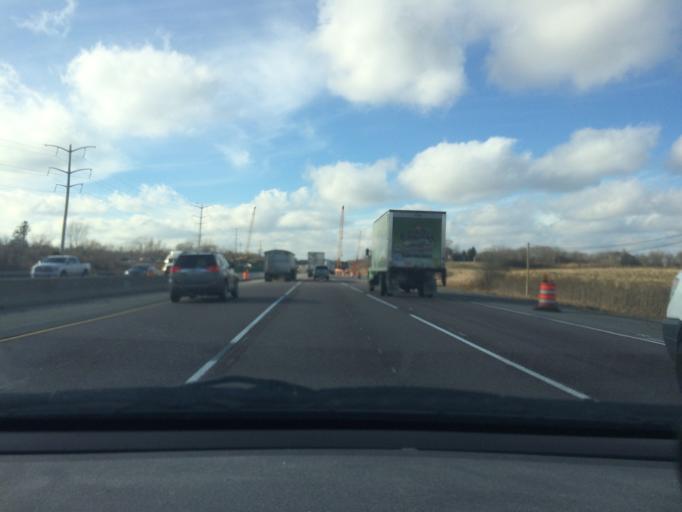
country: US
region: Illinois
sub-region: Cook County
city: South Barrington
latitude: 42.0666
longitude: -88.1549
